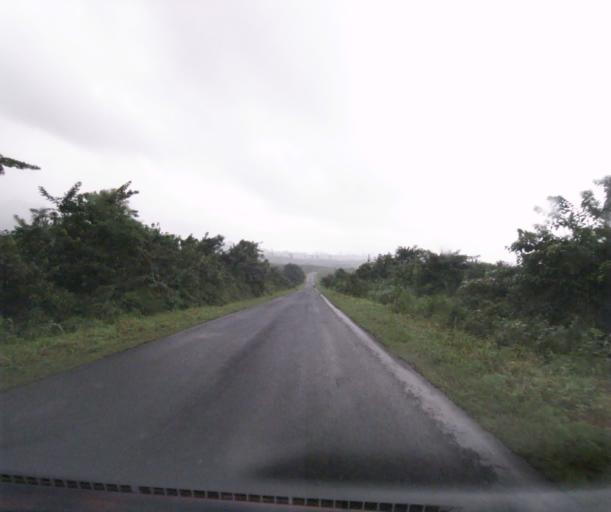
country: CM
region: South-West Province
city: Idenao
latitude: 4.1855
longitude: 9.0033
